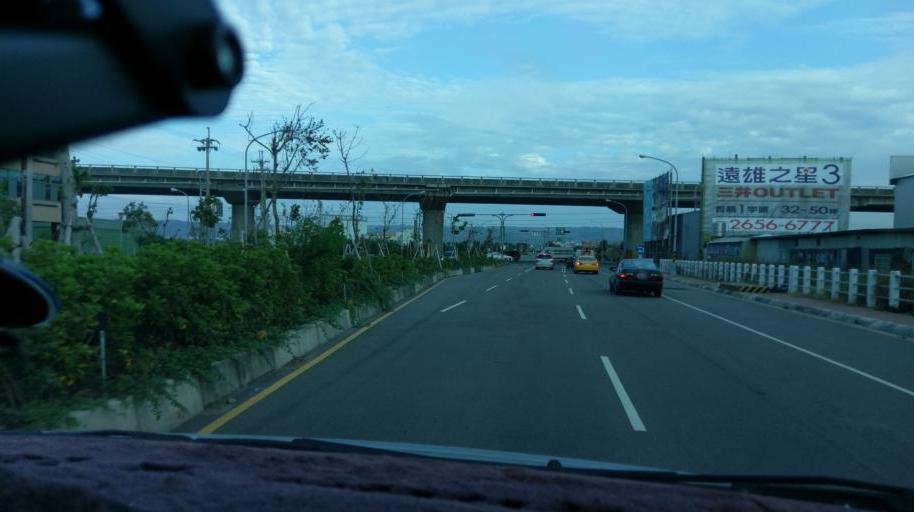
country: TW
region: Taiwan
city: Fengyuan
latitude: 24.2965
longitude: 120.5519
